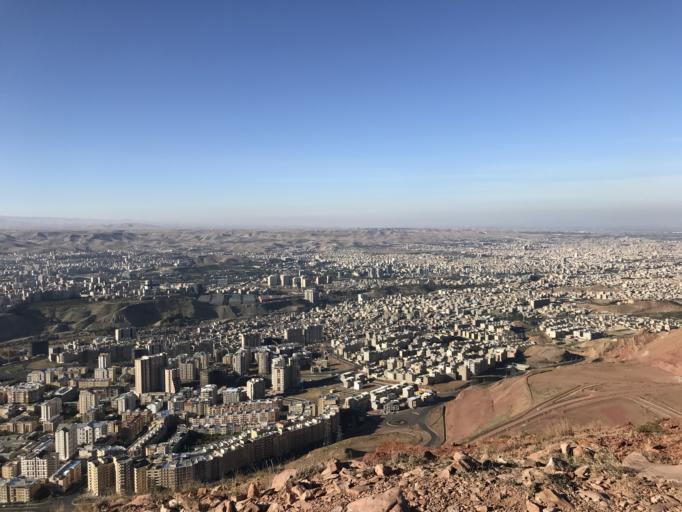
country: IR
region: East Azerbaijan
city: Tabriz
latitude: 38.0906
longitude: 46.3657
